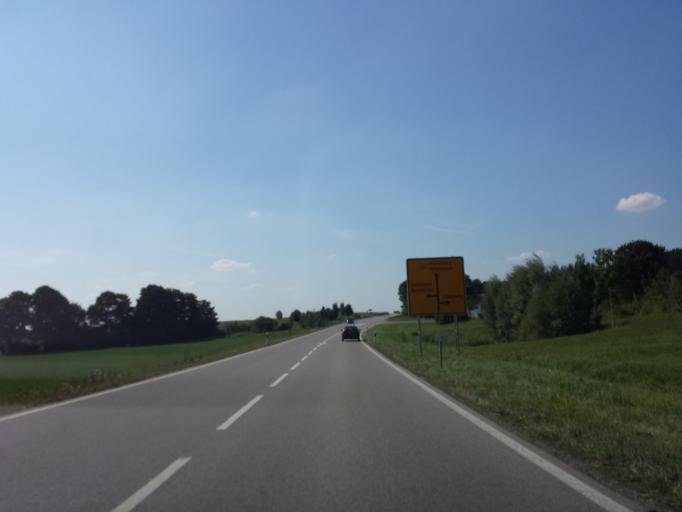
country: DE
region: Bavaria
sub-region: Swabia
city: Breitenbrunn
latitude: 48.1380
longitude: 10.4265
